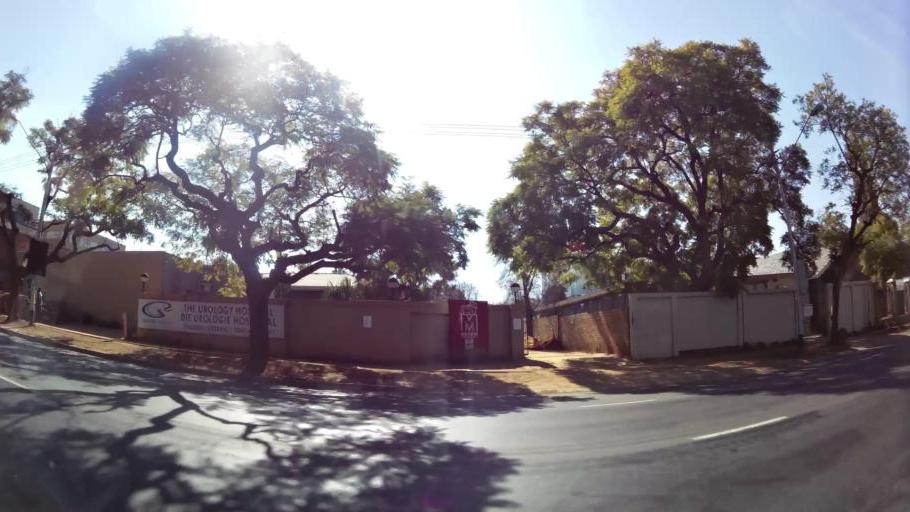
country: ZA
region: Gauteng
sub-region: City of Tshwane Metropolitan Municipality
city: Pretoria
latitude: -25.7445
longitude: 28.2384
